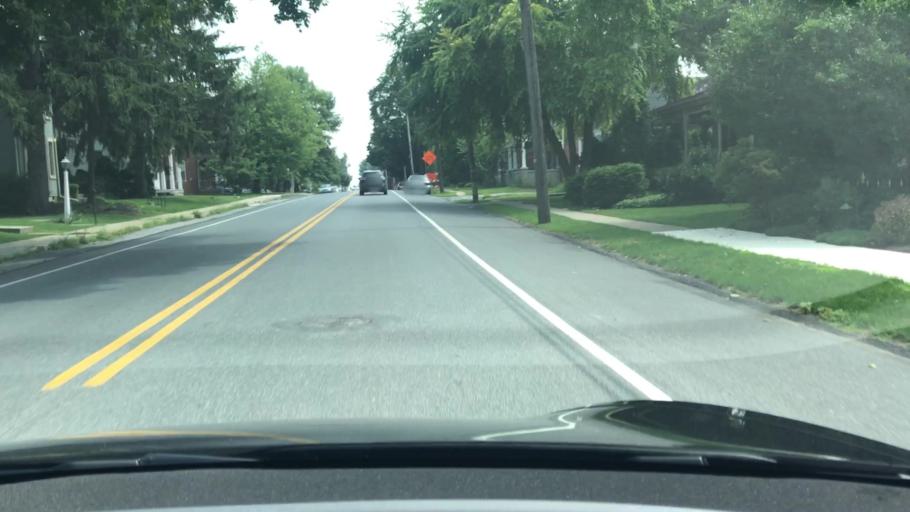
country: US
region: Pennsylvania
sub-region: Lancaster County
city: Landisville
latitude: 40.0968
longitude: -76.4144
